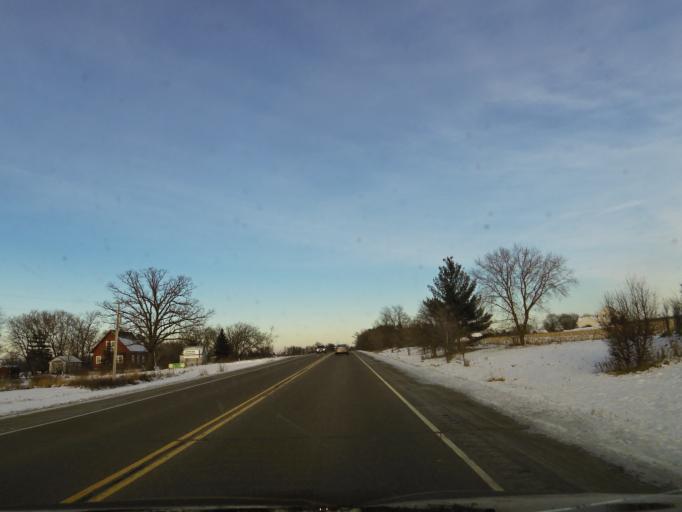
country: US
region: Wisconsin
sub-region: Polk County
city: Osceola
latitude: 45.3136
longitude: -92.7440
